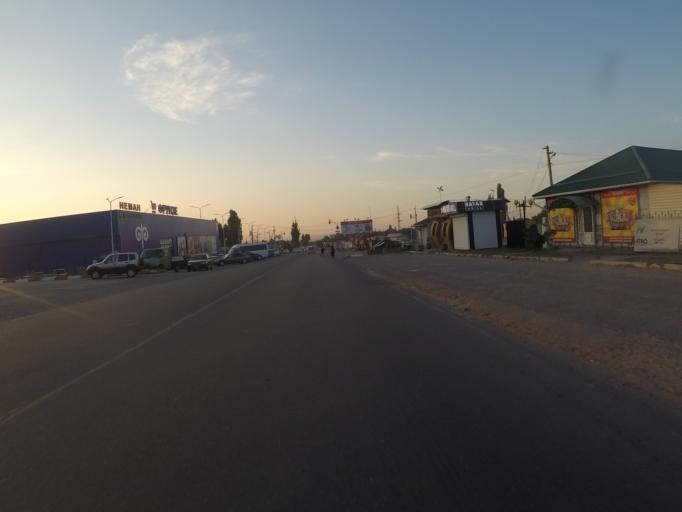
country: KG
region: Chuy
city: Lebedinovka
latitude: 42.8023
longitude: 74.6488
